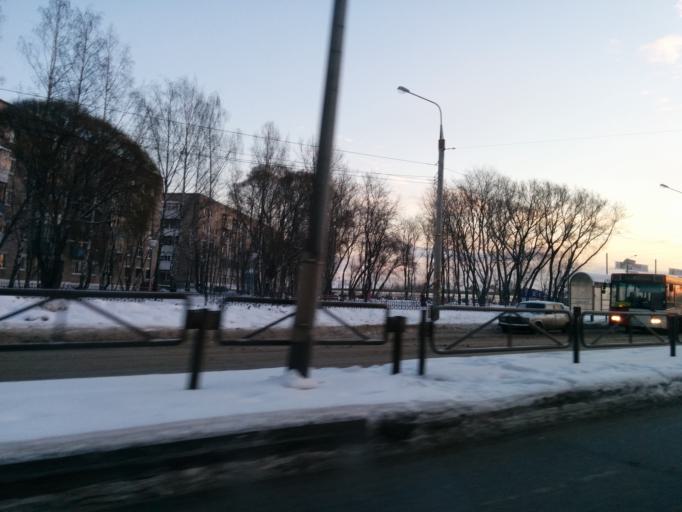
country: RU
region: Perm
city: Perm
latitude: 57.9909
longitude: 56.2954
